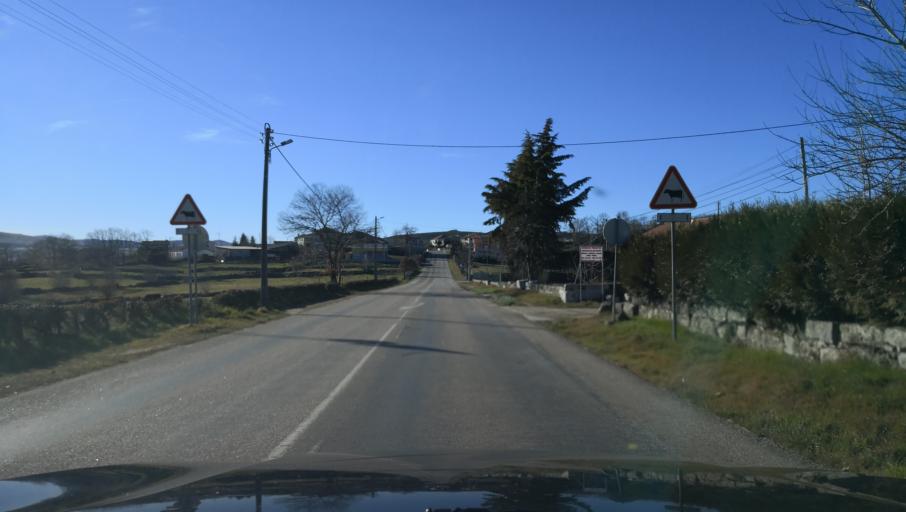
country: PT
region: Vila Real
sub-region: Vila Pouca de Aguiar
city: Vila Pouca de Aguiar
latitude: 41.5000
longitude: -7.7070
